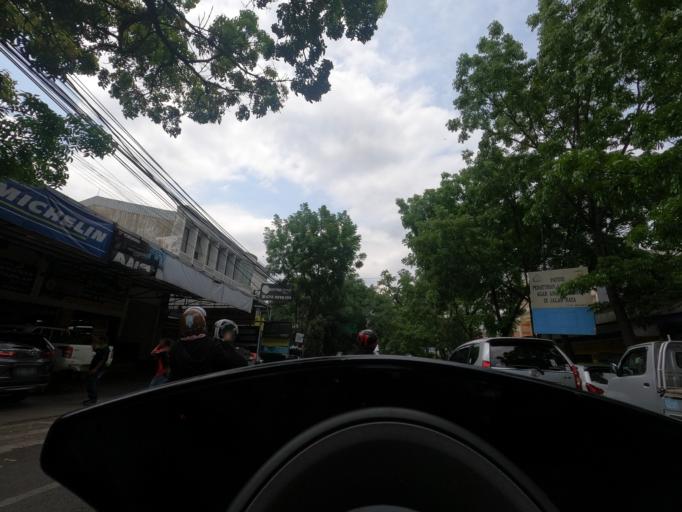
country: ID
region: West Java
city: Bandung
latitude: -6.9029
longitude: 107.6043
